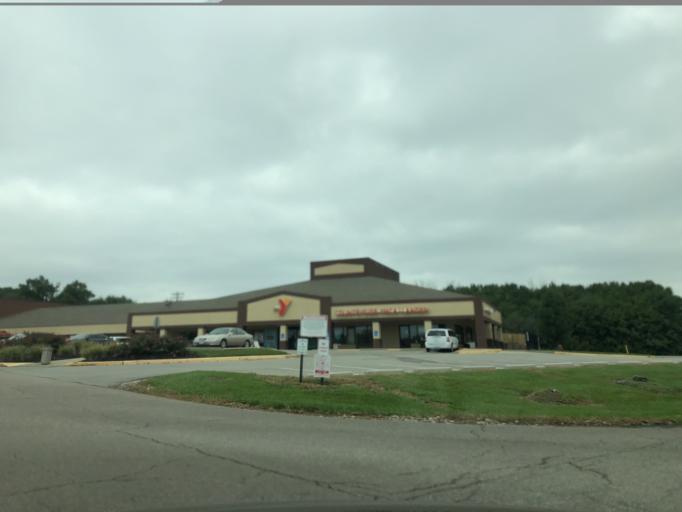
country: US
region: Ohio
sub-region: Warren County
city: Landen
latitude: 39.3110
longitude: -84.2732
